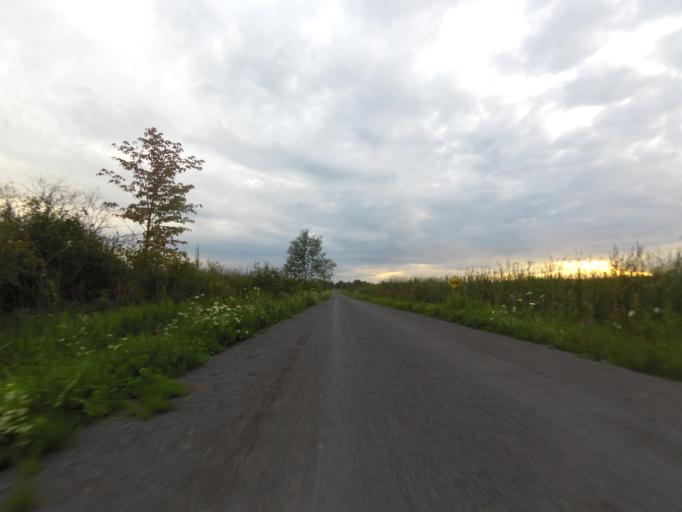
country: CA
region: Ontario
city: Carleton Place
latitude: 45.1876
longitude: -76.0327
